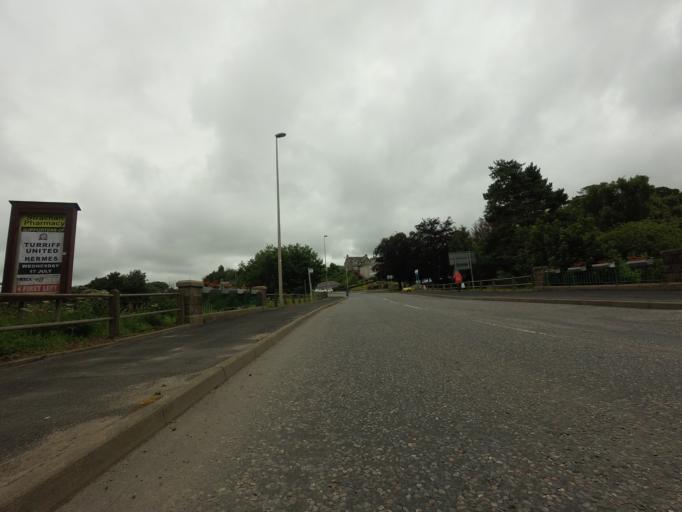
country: GB
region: Scotland
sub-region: Aberdeenshire
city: Turriff
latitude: 57.5345
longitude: -2.4620
